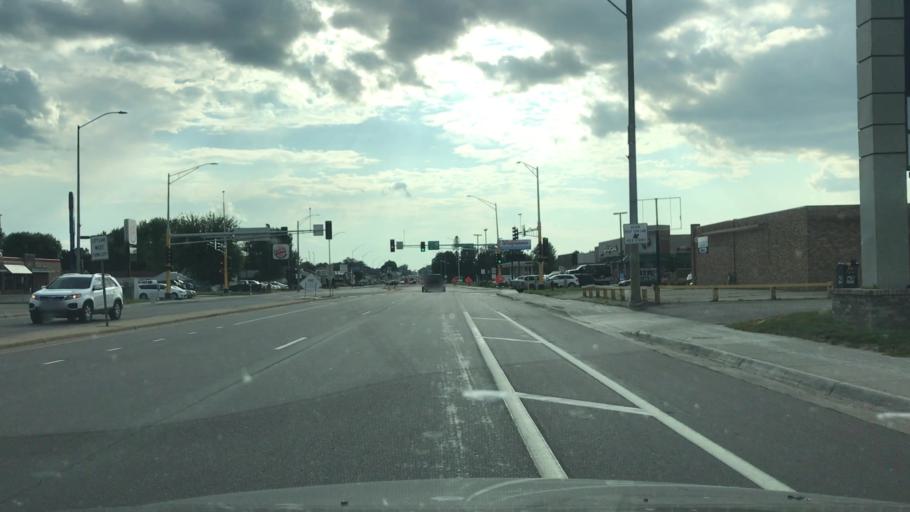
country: US
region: Minnesota
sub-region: Nobles County
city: Worthington
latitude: 43.6313
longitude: -95.5924
